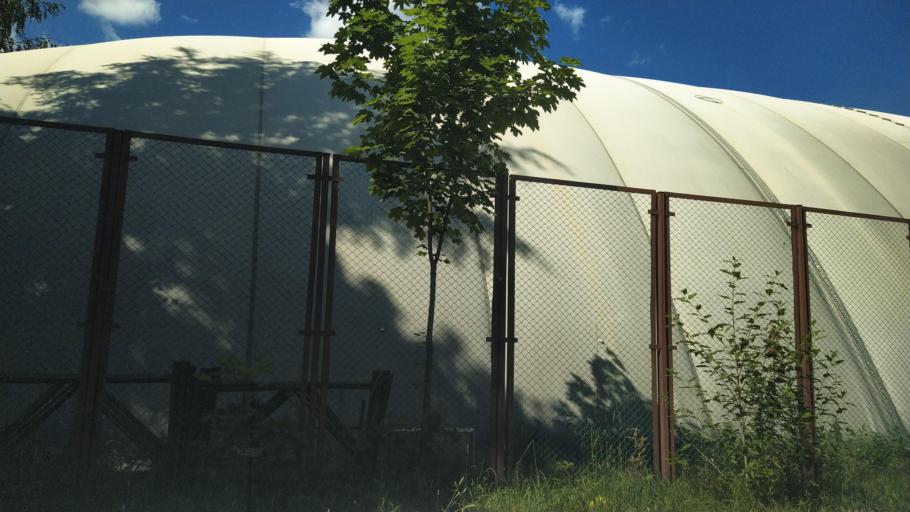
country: RU
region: St.-Petersburg
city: Ozerki
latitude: 60.0407
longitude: 30.3078
